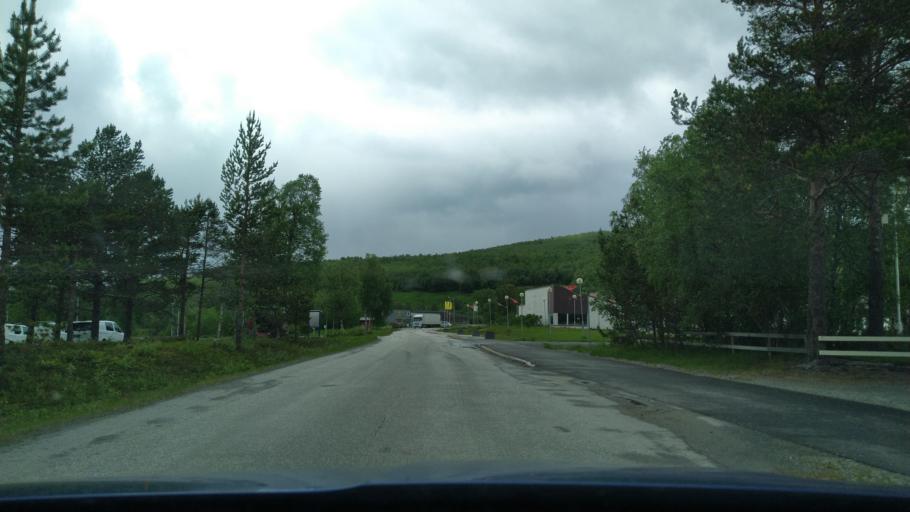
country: NO
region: Troms
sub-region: Dyroy
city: Brostadbotn
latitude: 69.0903
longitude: 17.6997
